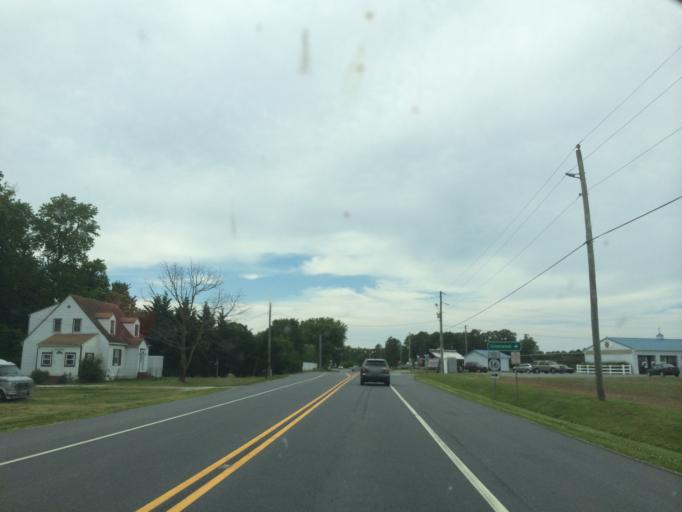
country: US
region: Delaware
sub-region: Sussex County
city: Bridgeville
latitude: 38.7798
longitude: -75.6661
